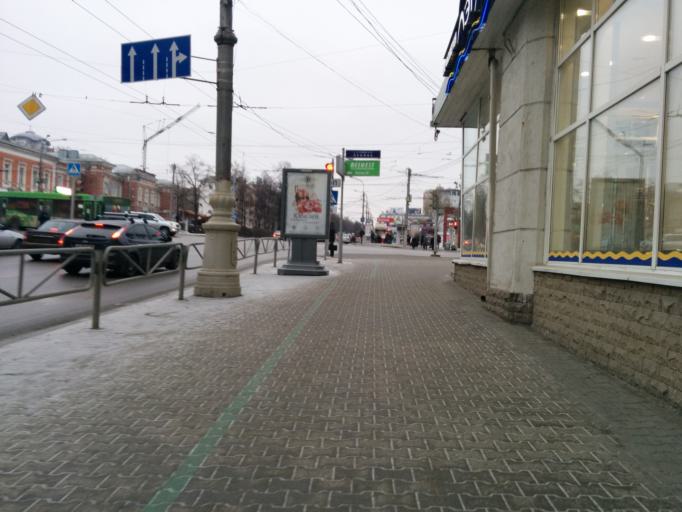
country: RU
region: Perm
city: Perm
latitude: 58.0117
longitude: 56.2380
